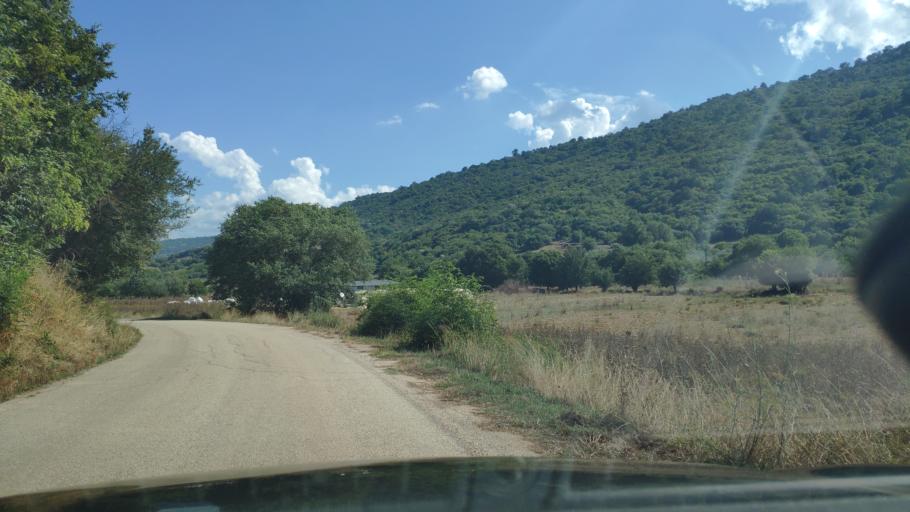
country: GR
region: West Greece
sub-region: Nomos Aitolias kai Akarnanias
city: Katouna
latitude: 38.8446
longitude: 21.0940
